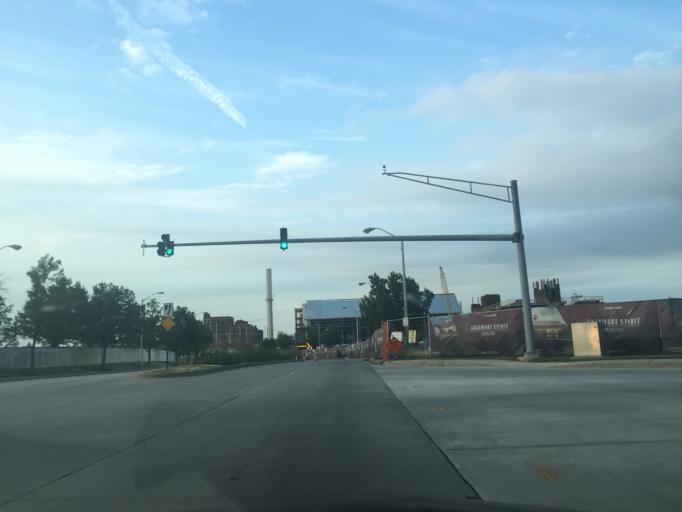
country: US
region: Maryland
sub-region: City of Baltimore
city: Baltimore
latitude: 39.2631
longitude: -76.6077
